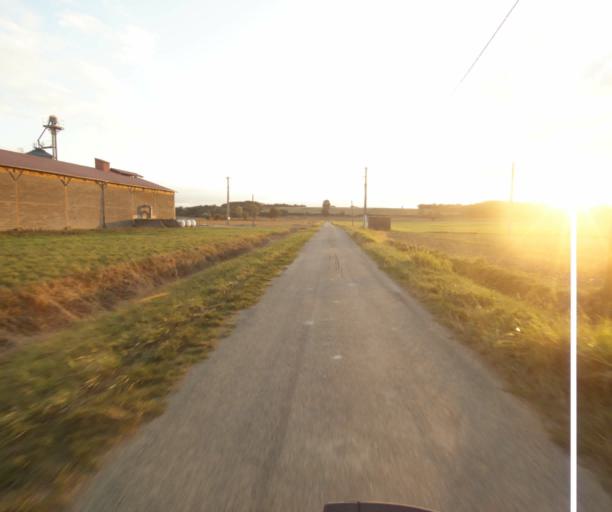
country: FR
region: Midi-Pyrenees
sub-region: Departement du Tarn-et-Garonne
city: Verdun-sur-Garonne
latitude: 43.8307
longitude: 1.2147
